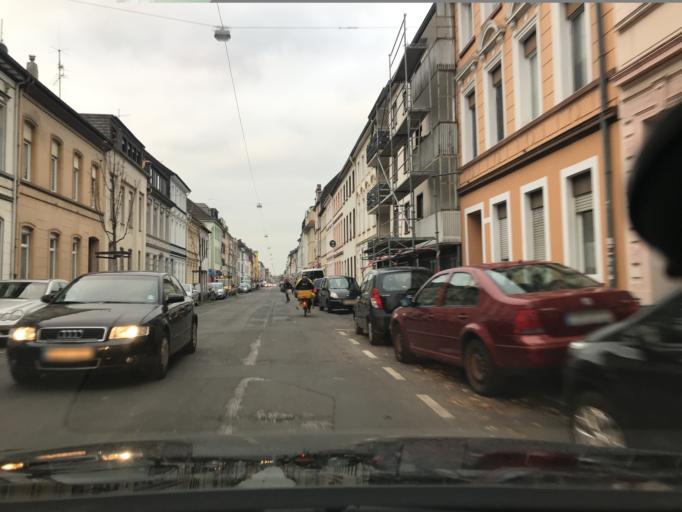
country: DE
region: North Rhine-Westphalia
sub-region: Regierungsbezirk Dusseldorf
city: Krefeld
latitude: 51.3279
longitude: 6.5589
